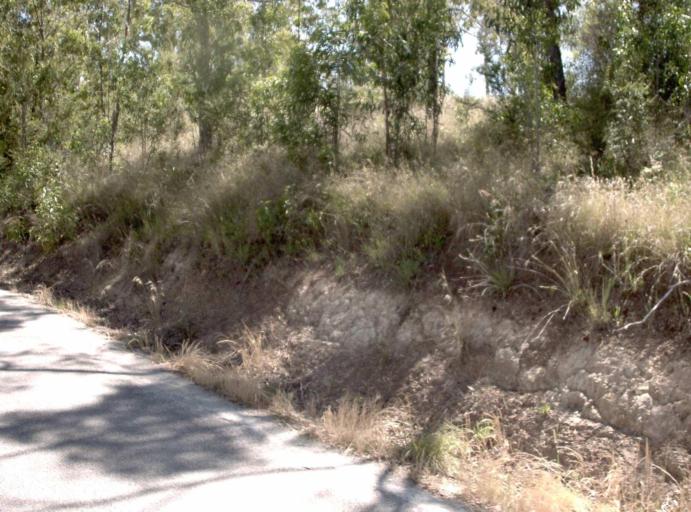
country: AU
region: Victoria
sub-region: East Gippsland
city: Lakes Entrance
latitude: -37.4546
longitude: 148.1932
